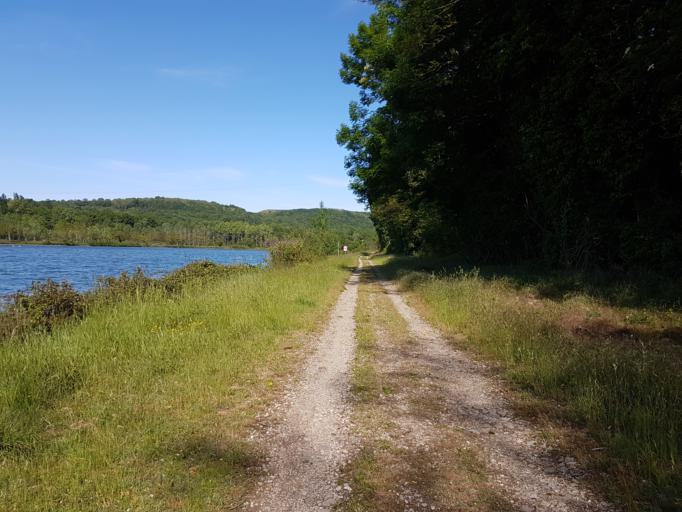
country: FR
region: Rhone-Alpes
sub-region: Departement de l'Ain
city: Villebois
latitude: 45.8392
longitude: 5.4228
